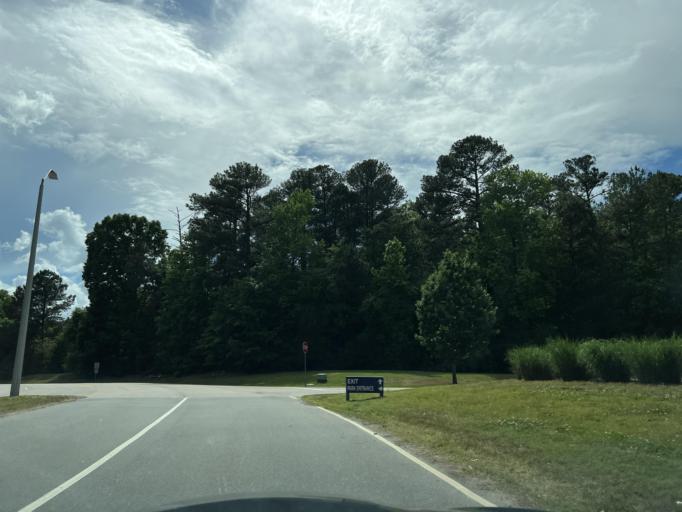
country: US
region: North Carolina
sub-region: Wake County
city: Wake Forest
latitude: 35.9054
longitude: -78.5835
